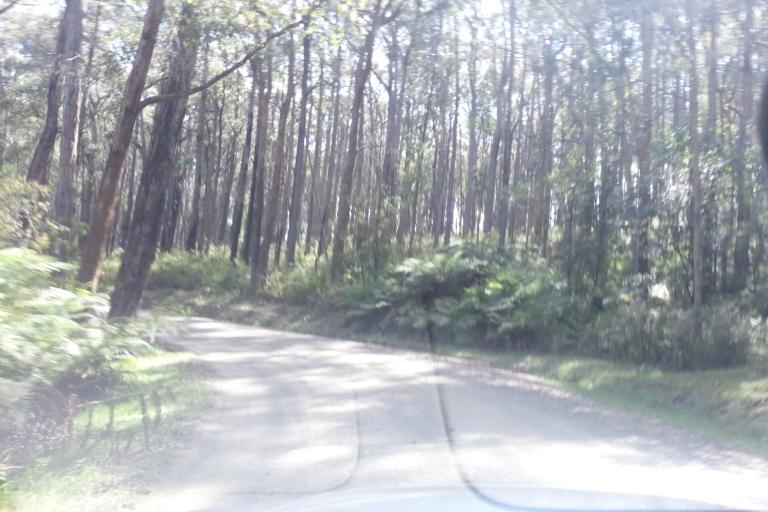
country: AU
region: Victoria
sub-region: Cardinia
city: Gembrook
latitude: -37.9399
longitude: 145.5859
